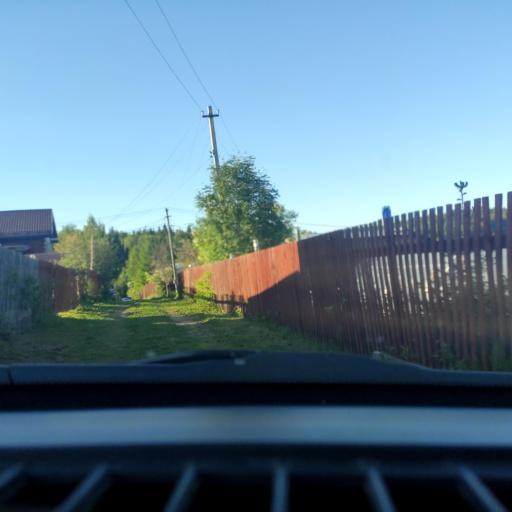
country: RU
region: Perm
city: Ferma
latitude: 57.9681
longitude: 56.3905
